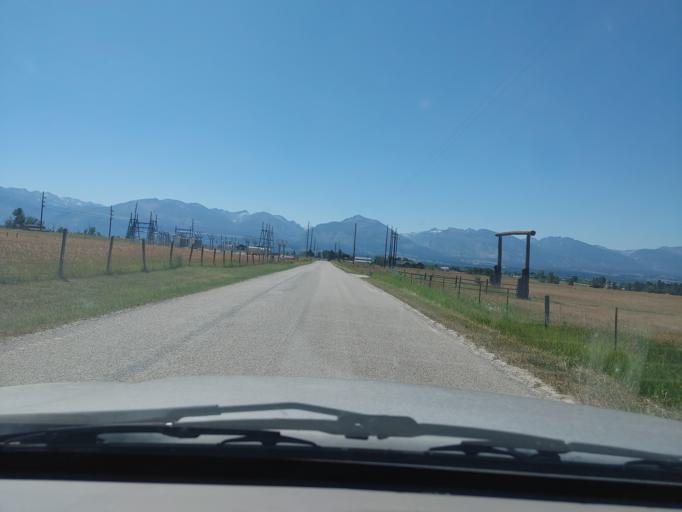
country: US
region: Montana
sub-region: Ravalli County
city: Hamilton
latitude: 46.2766
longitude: -114.0307
